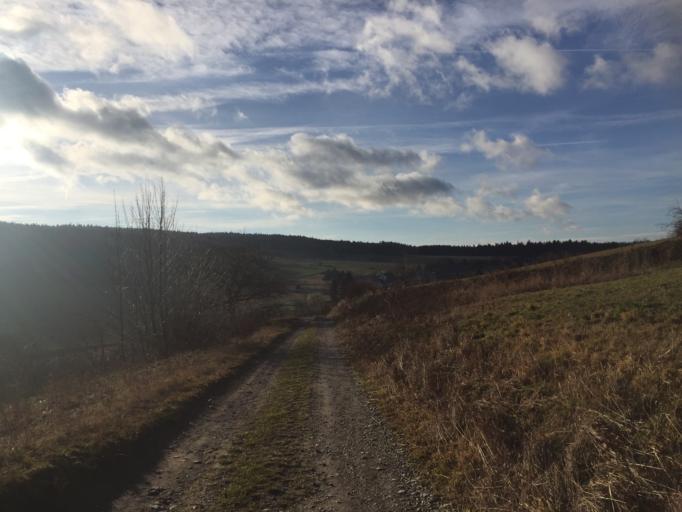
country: DE
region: Thuringia
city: Doschnitz
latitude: 50.6550
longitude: 11.2420
